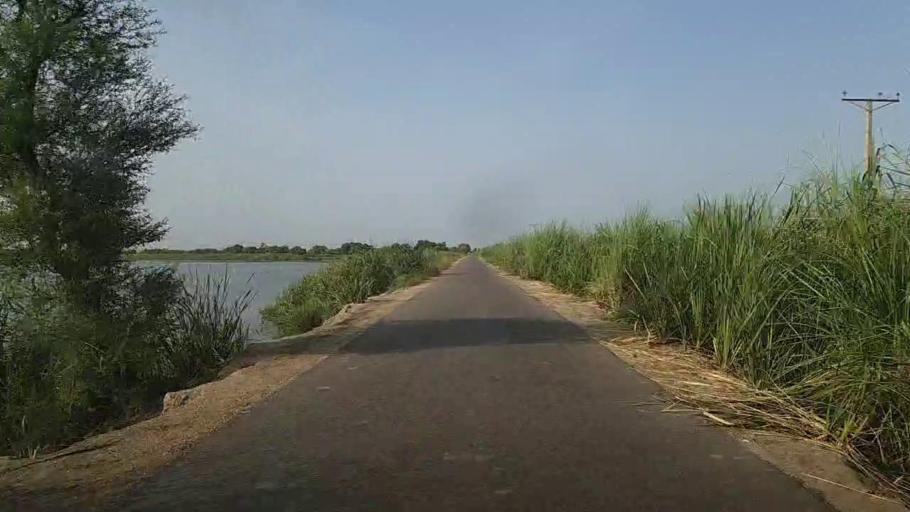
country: PK
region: Sindh
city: Khairpur
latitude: 28.0809
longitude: 69.8143
